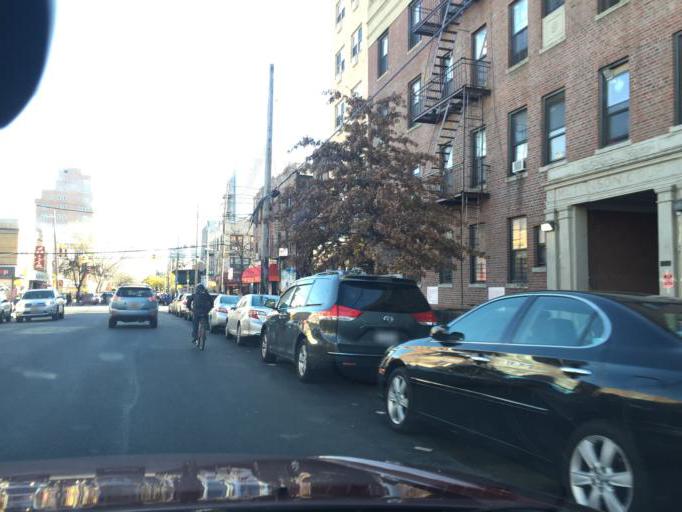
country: US
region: New York
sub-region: Kings County
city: Bensonhurst
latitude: 40.6359
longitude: -74.0103
